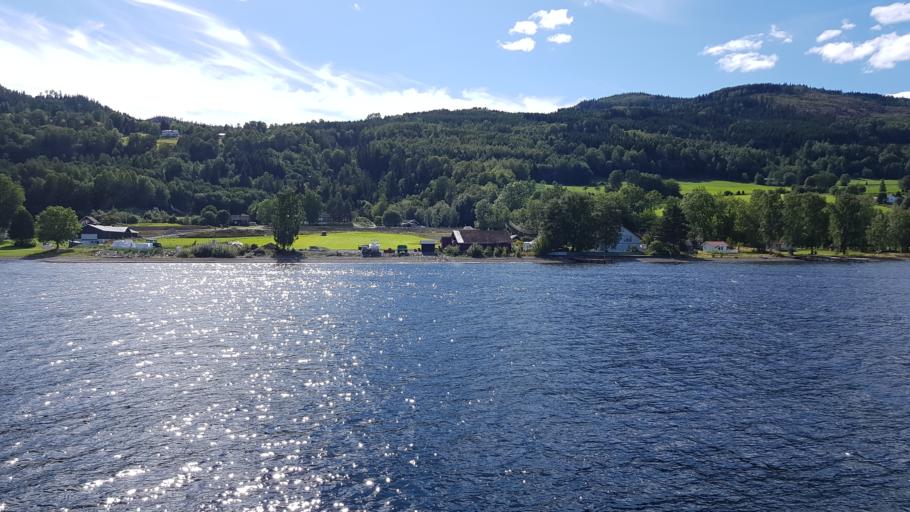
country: NO
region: Hedmark
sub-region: Stange
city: Stange
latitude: 60.6330
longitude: 11.0930
